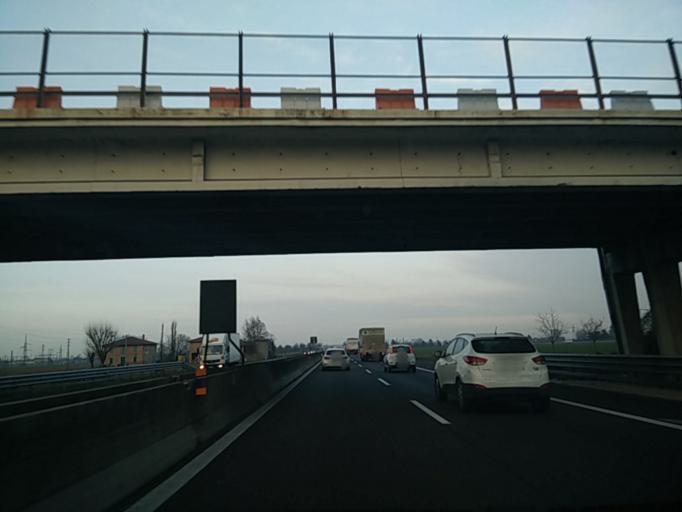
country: IT
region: Emilia-Romagna
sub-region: Provincia di Bologna
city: Progresso
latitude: 44.5697
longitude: 11.3859
